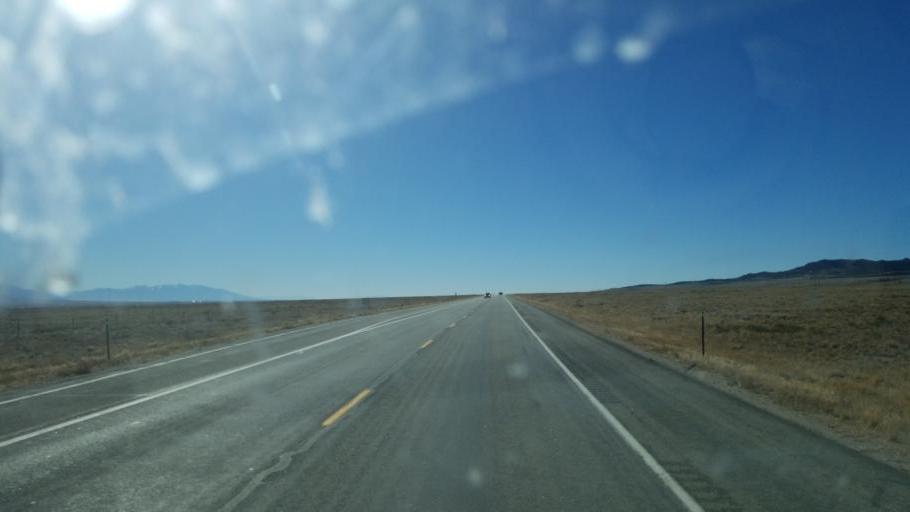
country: US
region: Colorado
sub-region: Saguache County
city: Saguache
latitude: 38.2410
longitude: -105.9457
